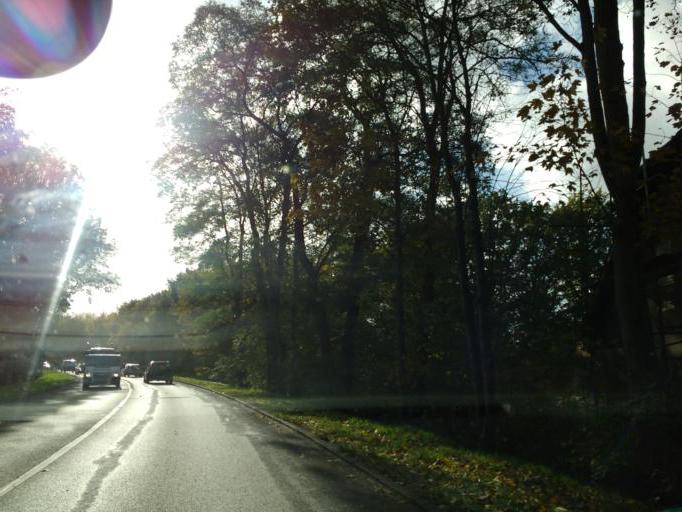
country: DE
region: Brandenburg
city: Petershagen
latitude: 52.5336
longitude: 13.8192
